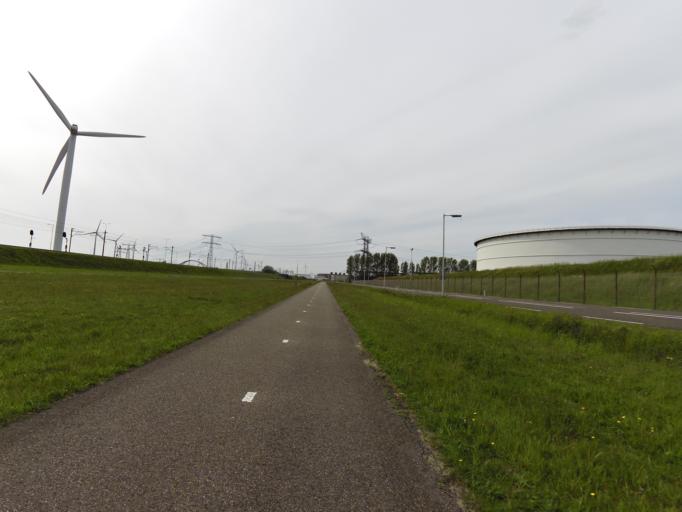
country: NL
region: South Holland
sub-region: Gemeente Brielle
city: Brielle
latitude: 51.9347
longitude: 4.1560
